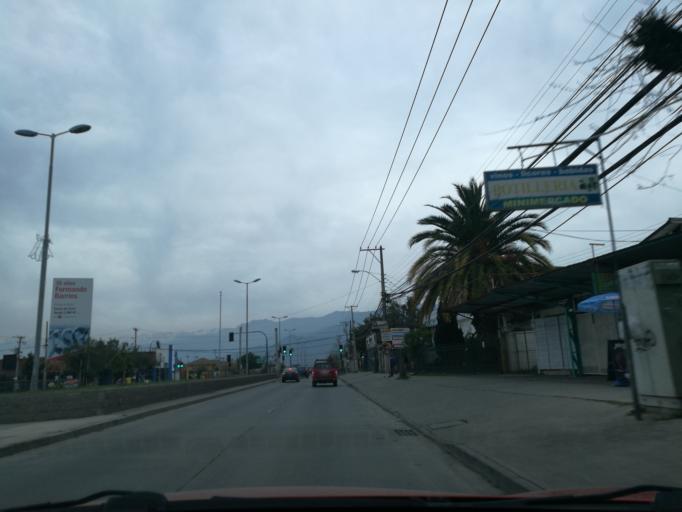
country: CL
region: O'Higgins
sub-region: Provincia de Cachapoal
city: Machali
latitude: -34.1739
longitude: -70.6893
